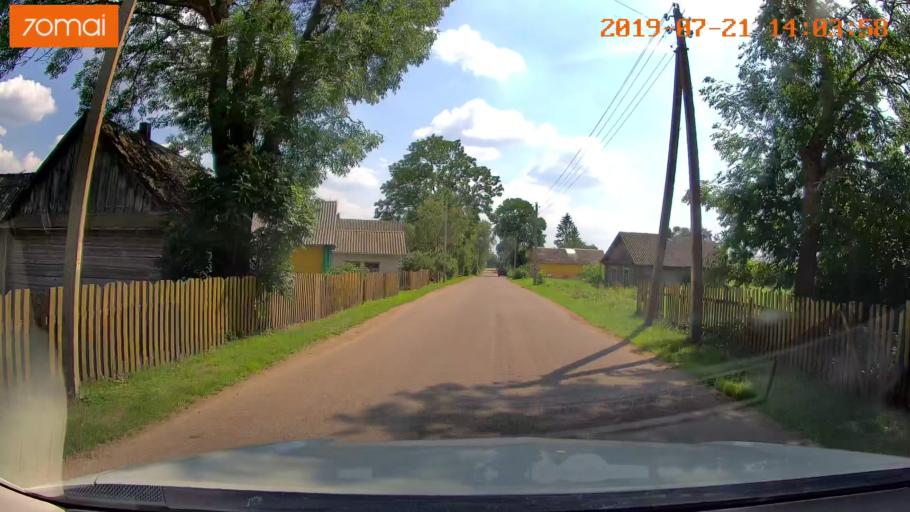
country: BY
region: Grodnenskaya
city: Lyubcha
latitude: 53.7247
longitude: 26.0953
